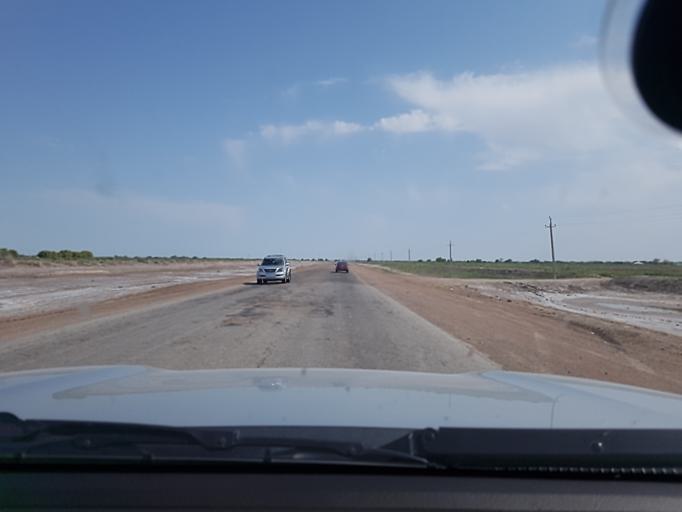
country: TM
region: Dasoguz
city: Boldumsaz
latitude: 42.1858
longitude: 59.5649
